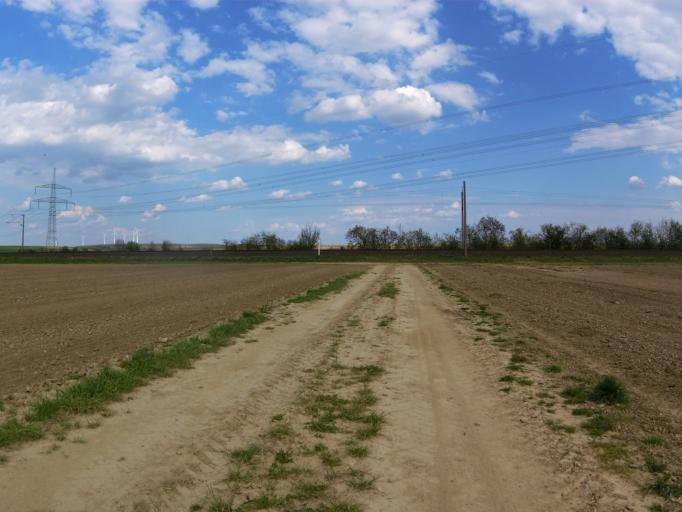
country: DE
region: Bavaria
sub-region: Regierungsbezirk Unterfranken
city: Oberpleichfeld
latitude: 49.8655
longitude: 10.0994
